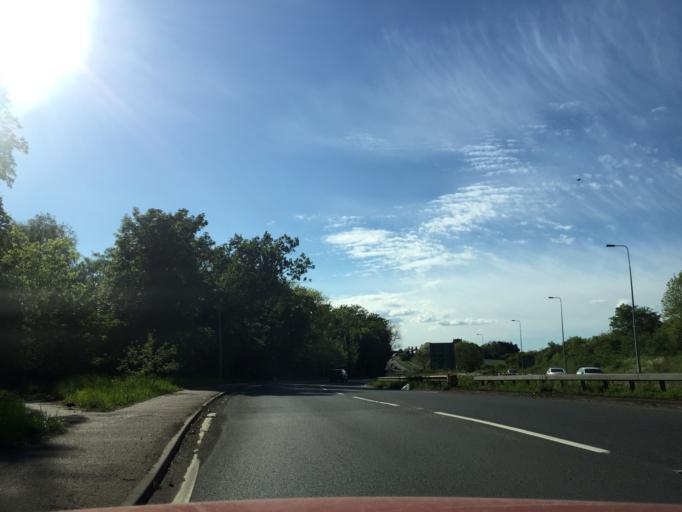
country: GB
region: England
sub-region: Warwickshire
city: Ryton on Dunsmore
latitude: 52.3643
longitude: -1.4271
